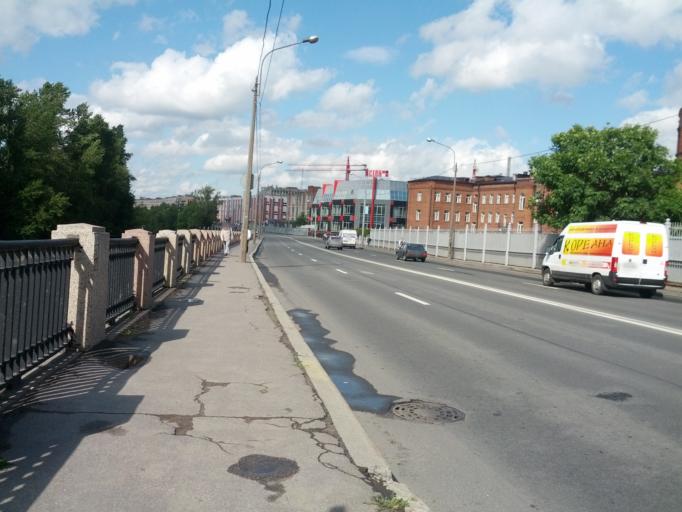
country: RU
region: St.-Petersburg
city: Centralniy
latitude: 59.9343
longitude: 30.4155
